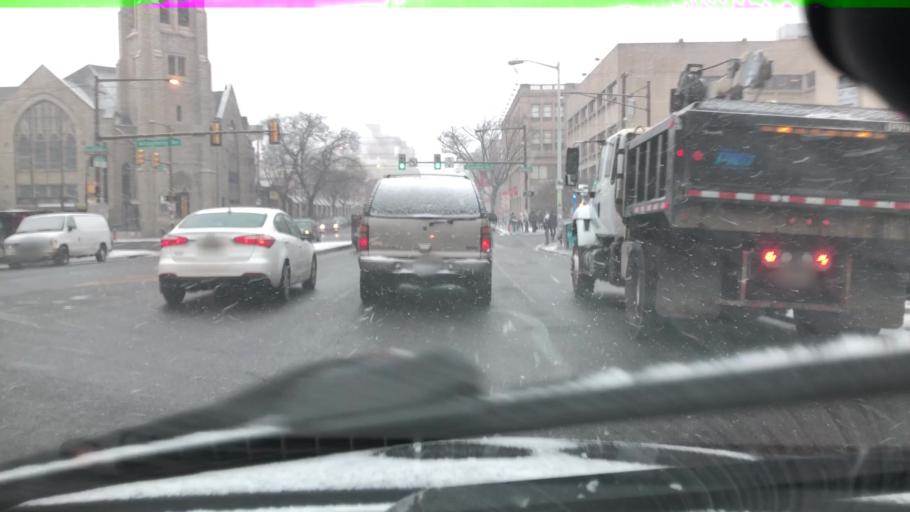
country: US
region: Pennsylvania
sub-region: Philadelphia County
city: Philadelphia
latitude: 40.0010
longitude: -75.1530
